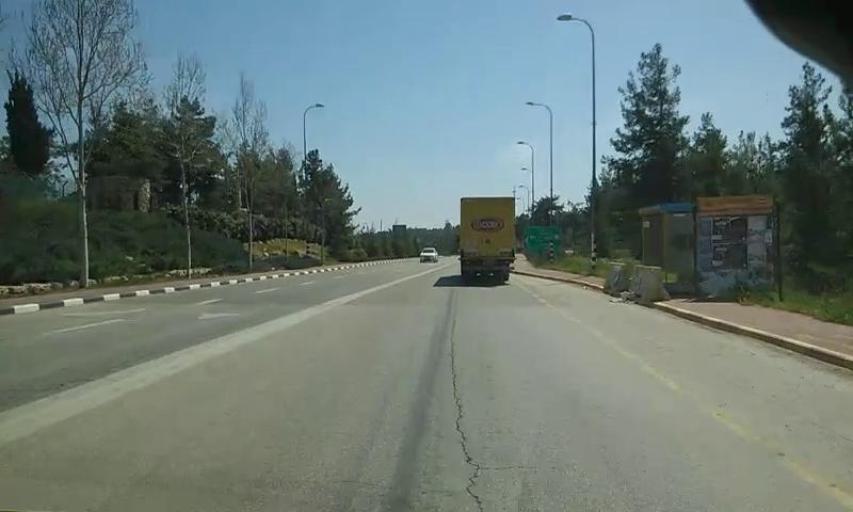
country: PS
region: West Bank
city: Shuyukh al `Arrub
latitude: 31.6481
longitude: 35.1293
